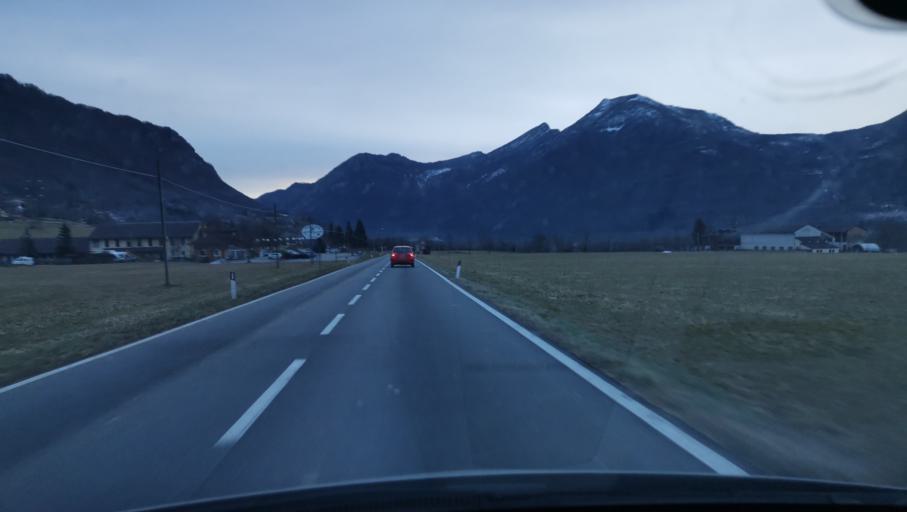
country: IT
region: Piedmont
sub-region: Provincia di Cuneo
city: Demonte
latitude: 44.3146
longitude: 7.3273
